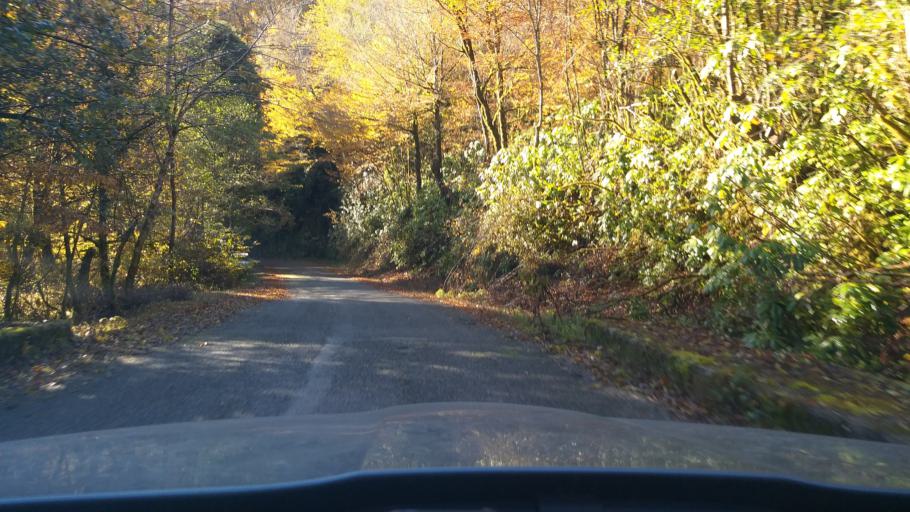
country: GE
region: Abkhazia
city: Bich'vinta
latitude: 43.1880
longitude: 40.4531
